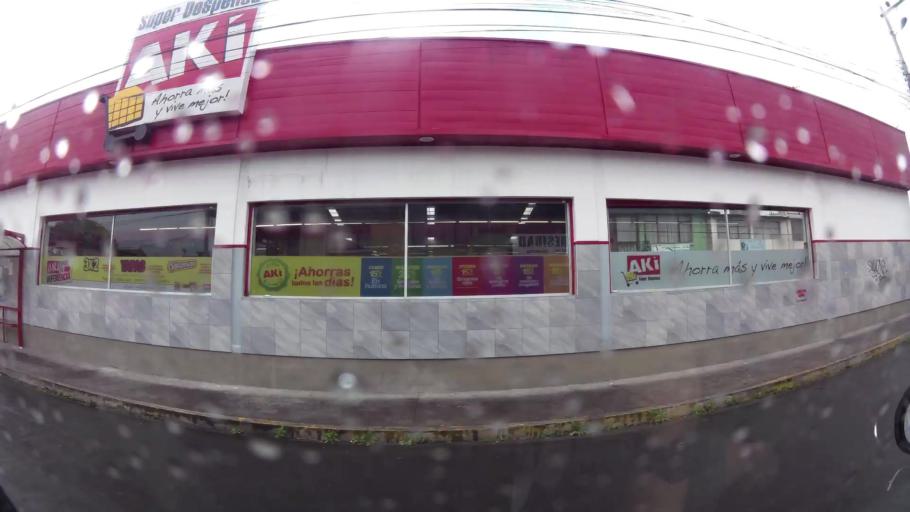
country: EC
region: Pichincha
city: Sangolqui
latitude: -0.2954
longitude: -78.4796
